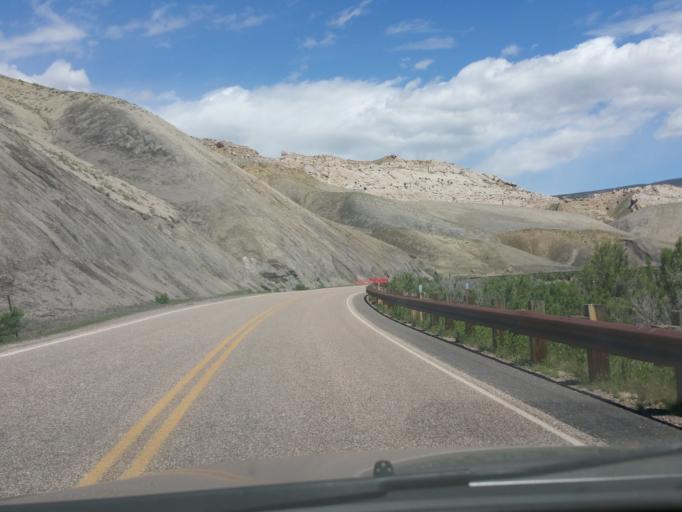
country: US
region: Utah
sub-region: Uintah County
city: Naples
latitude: 40.4351
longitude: -109.3297
